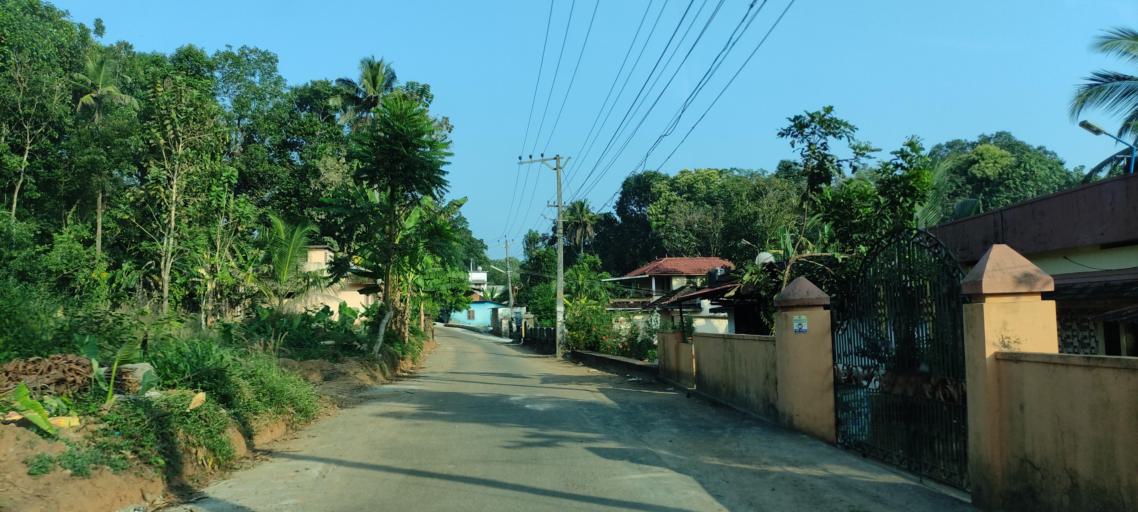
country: IN
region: Kerala
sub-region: Pattanamtitta
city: Adur
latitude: 9.1545
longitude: 76.7471
